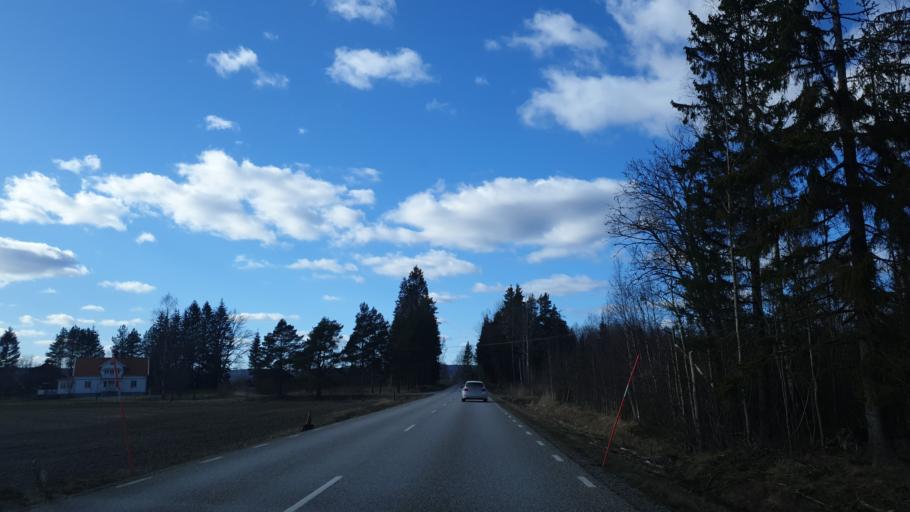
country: SE
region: OErebro
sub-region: Orebro Kommun
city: Garphyttan
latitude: 59.3363
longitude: 15.0734
